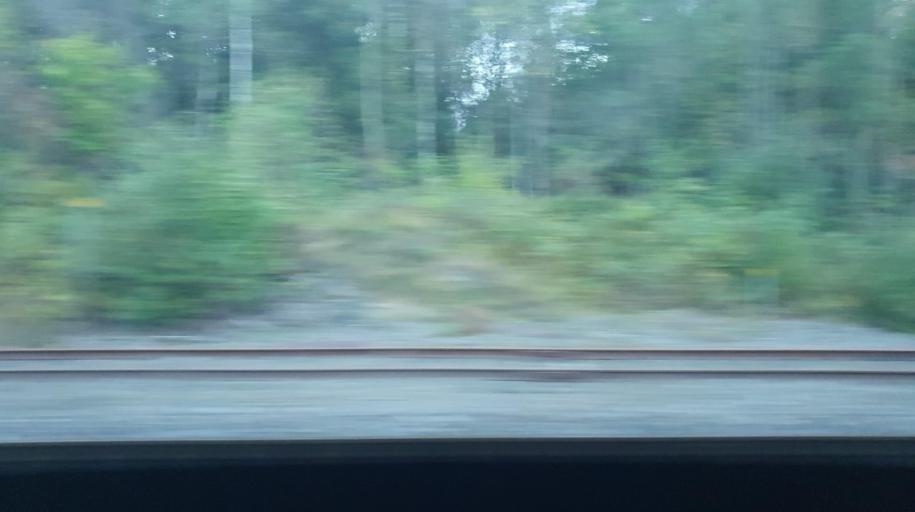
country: NO
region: Vestfold
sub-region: Horten
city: Skoppum
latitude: 59.3929
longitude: 10.4114
